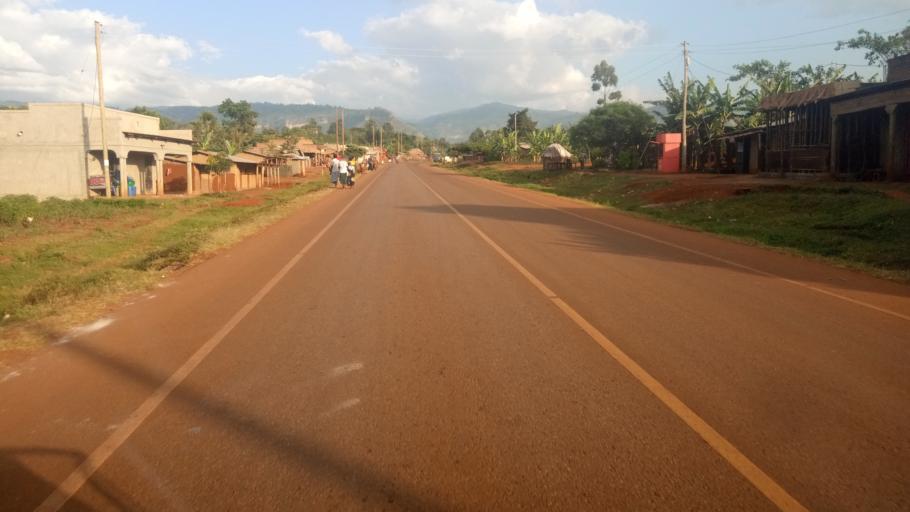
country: UG
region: Eastern Region
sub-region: Sironko District
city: Sironko
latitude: 1.3221
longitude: 34.3348
